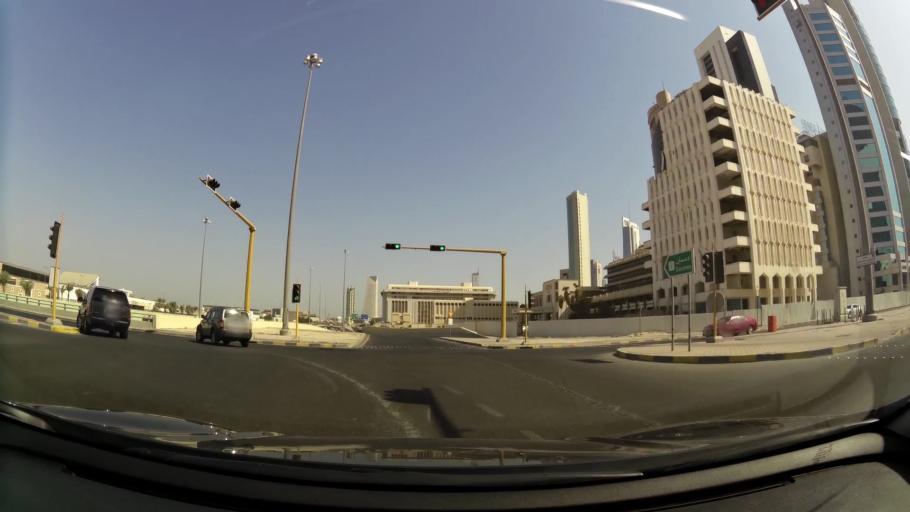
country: KW
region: Al Asimah
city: Kuwait City
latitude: 29.3670
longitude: 47.9644
